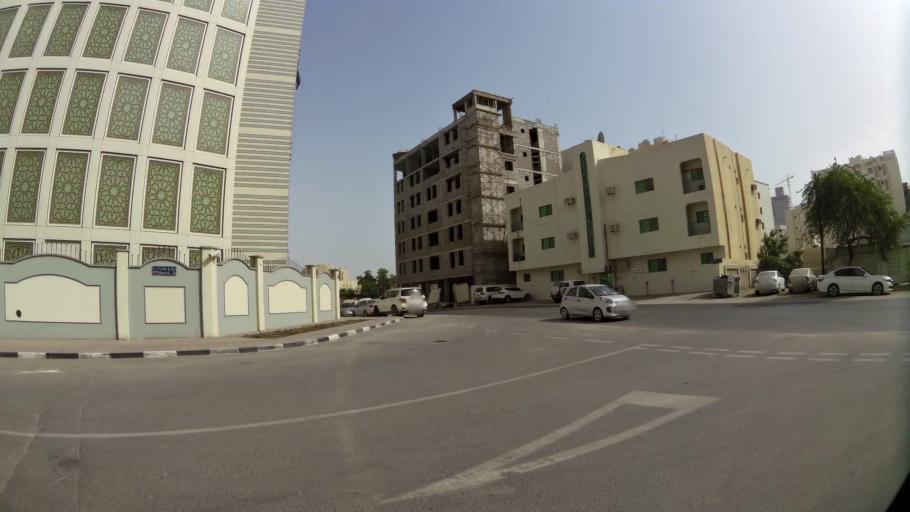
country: QA
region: Baladiyat ad Dawhah
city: Doha
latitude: 25.2828
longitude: 51.5099
